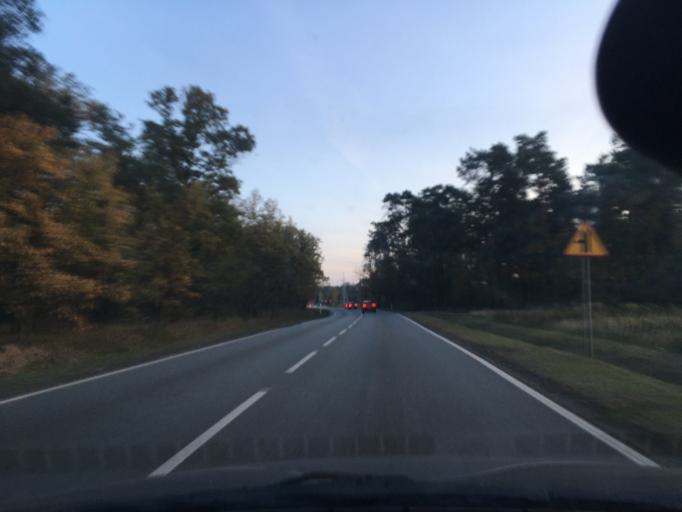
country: PL
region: Masovian Voivodeship
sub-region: Powiat sochaczewski
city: Mlodzieszyn
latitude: 52.3375
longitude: 20.2146
